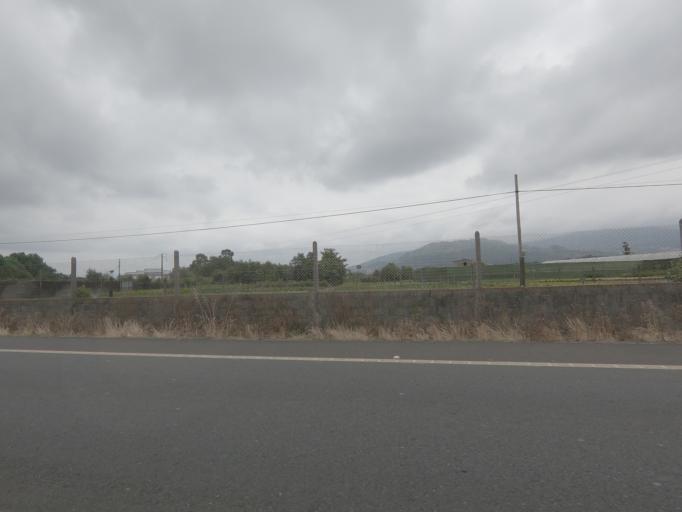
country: ES
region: Galicia
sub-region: Provincia de Pontevedra
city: Tomino
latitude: 41.9611
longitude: -8.7627
